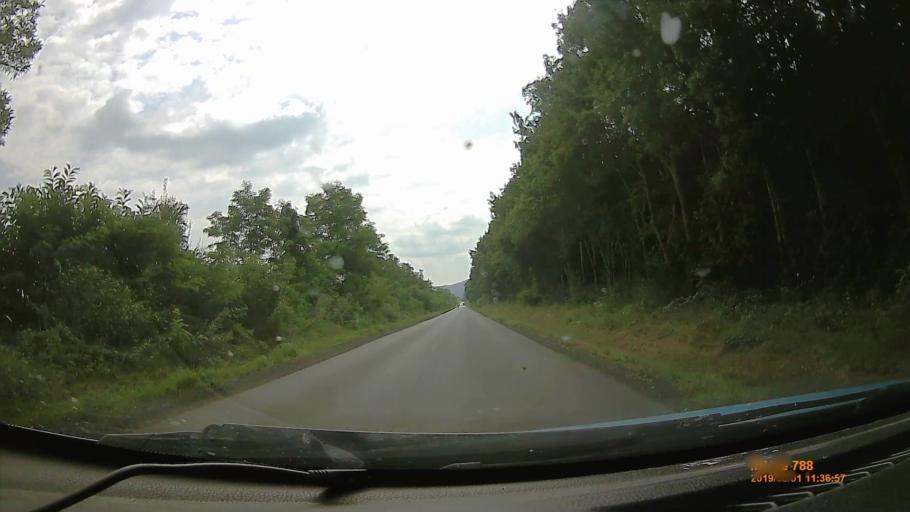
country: HU
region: Baranya
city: Villany
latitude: 45.9118
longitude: 18.3793
